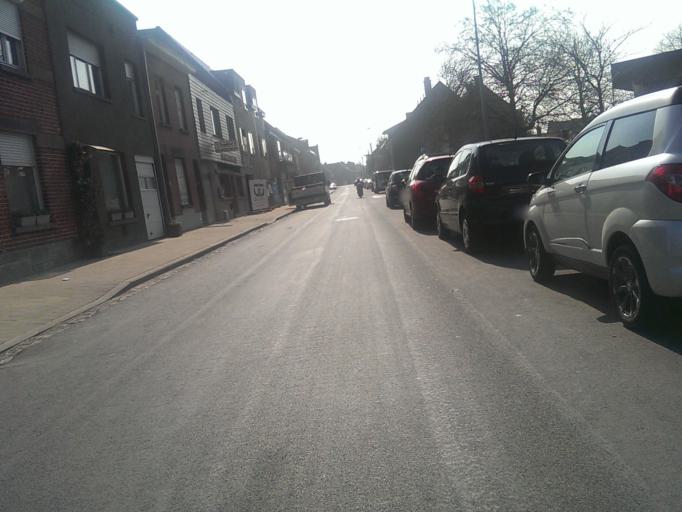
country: BE
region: Flanders
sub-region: Provincie West-Vlaanderen
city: Roeselare
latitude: 50.9374
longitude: 3.1258
